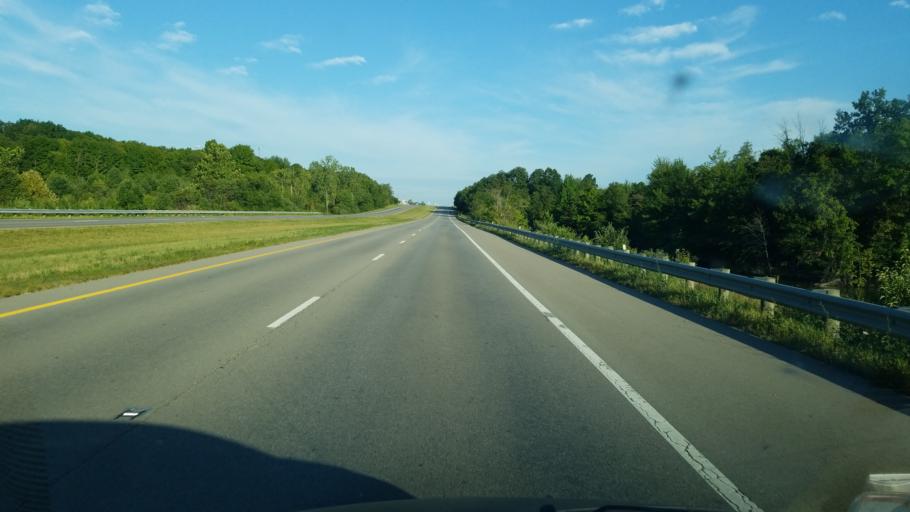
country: US
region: Ohio
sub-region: Delaware County
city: Lewis Center
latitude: 40.2697
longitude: -82.9532
